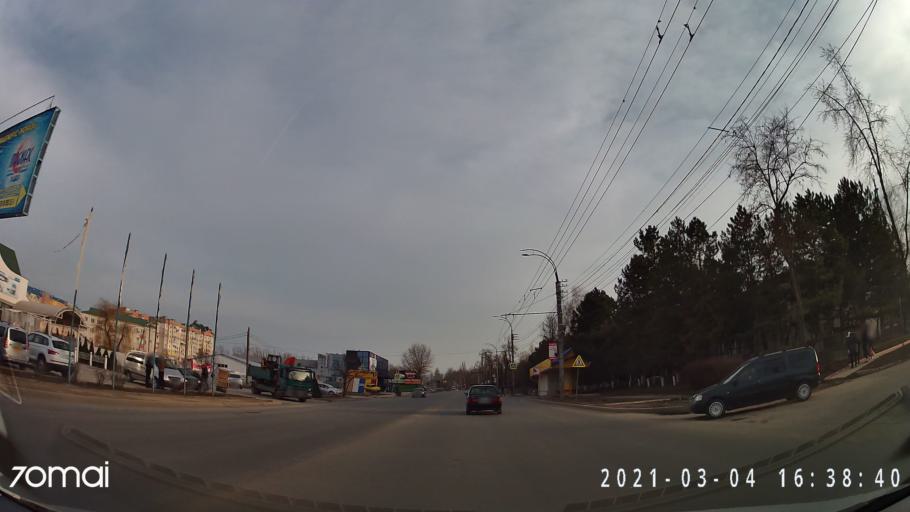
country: MD
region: Balti
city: Balti
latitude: 47.7796
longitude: 27.8922
